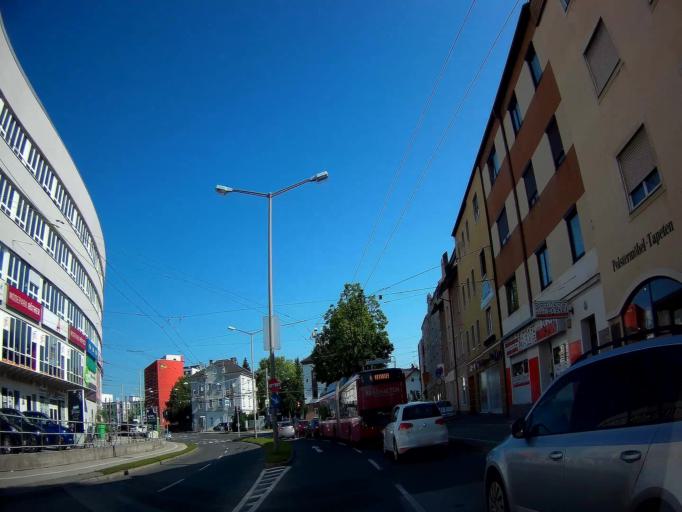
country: TN
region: Qibili
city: Douz
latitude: 33.4659
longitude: 9.1461
